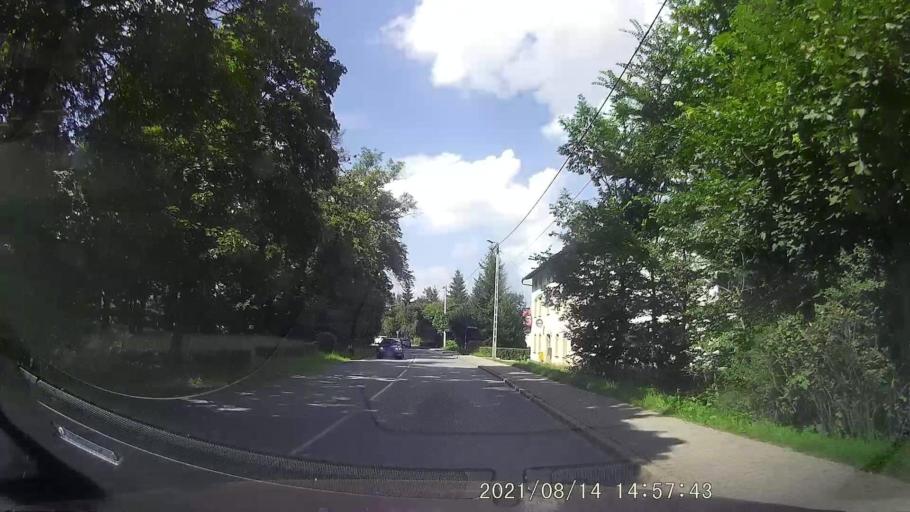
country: PL
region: Lower Silesian Voivodeship
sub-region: Powiat walbrzyski
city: Gluszyca
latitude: 50.6991
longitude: 16.3672
